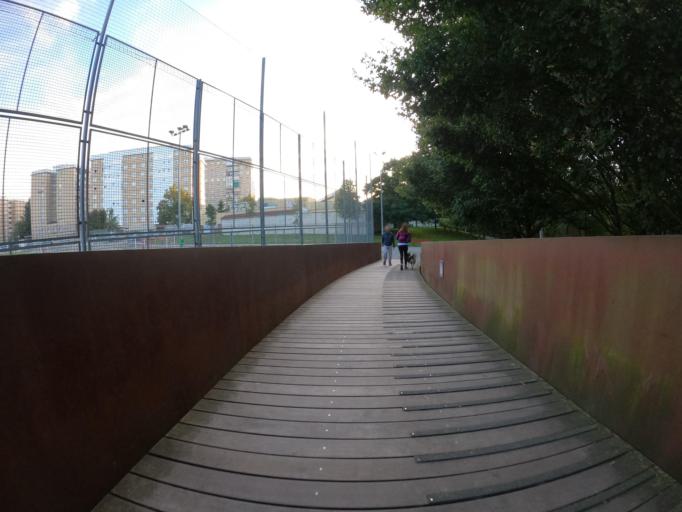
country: ES
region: Navarre
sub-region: Provincia de Navarra
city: Ermitagana
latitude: 42.8186
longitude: -1.6724
